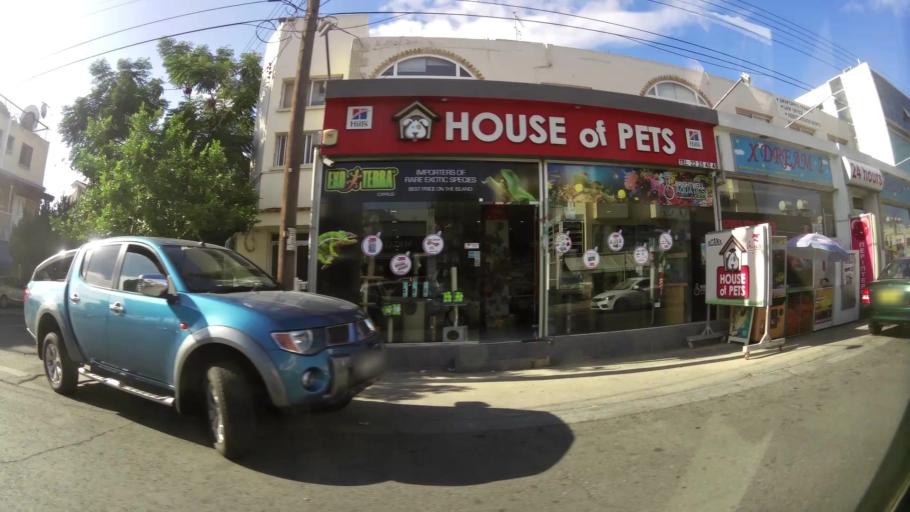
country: CY
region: Lefkosia
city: Nicosia
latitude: 35.1374
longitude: 33.3496
